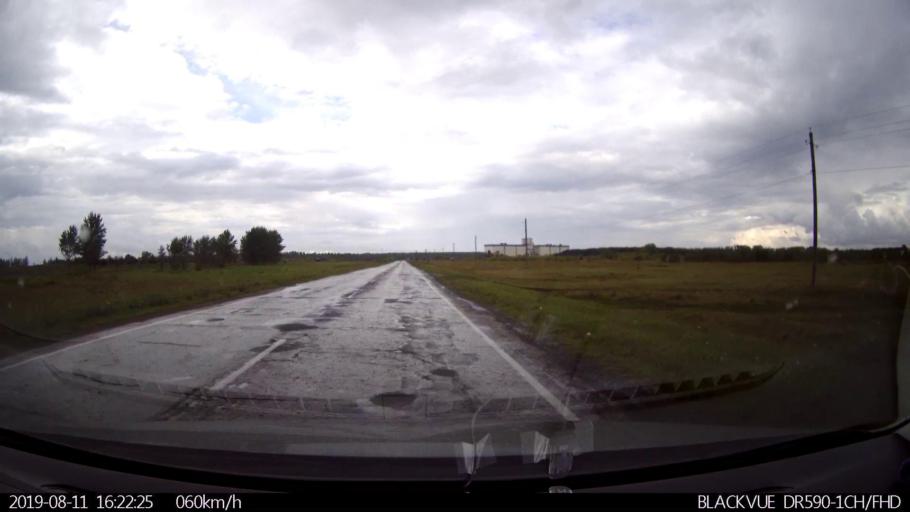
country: RU
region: Ulyanovsk
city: Mayna
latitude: 54.0878
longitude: 47.5931
